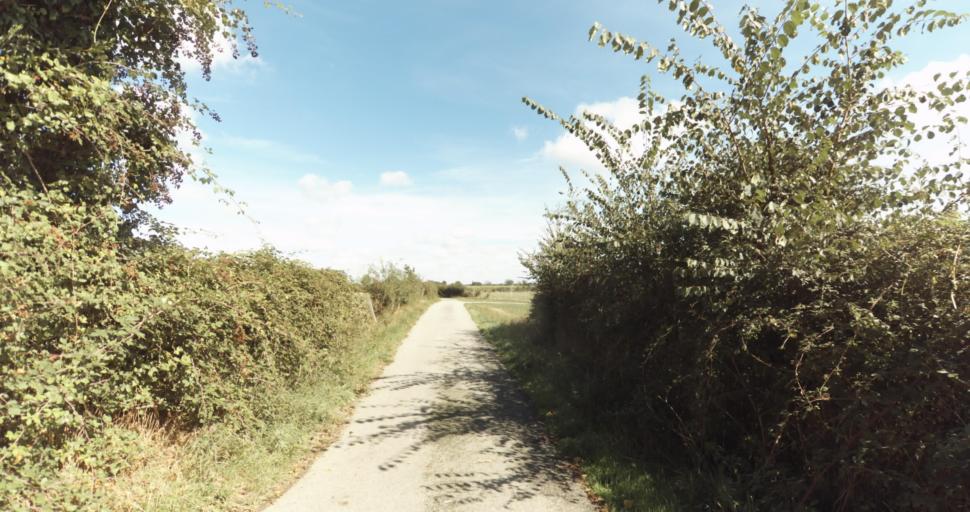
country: FR
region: Lower Normandy
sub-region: Departement du Calvados
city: Orbec
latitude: 48.9445
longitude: 0.3996
